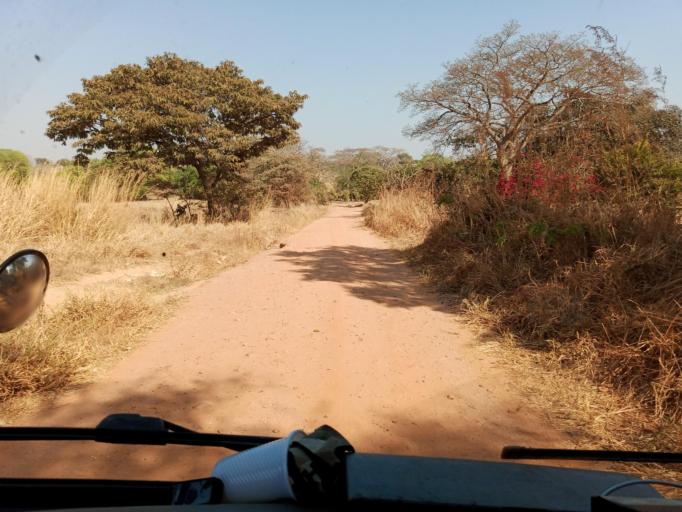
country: ZM
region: Lusaka
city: Lusaka
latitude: -15.3382
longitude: 28.2036
